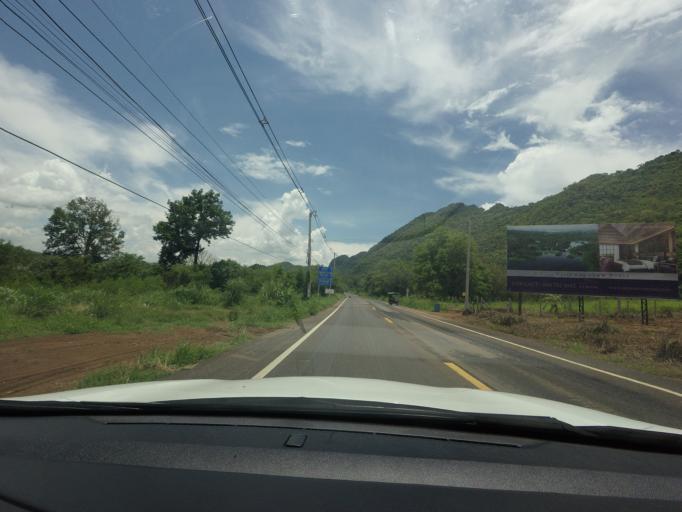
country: TH
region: Sara Buri
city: Muak Lek
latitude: 14.5799
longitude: 101.2602
